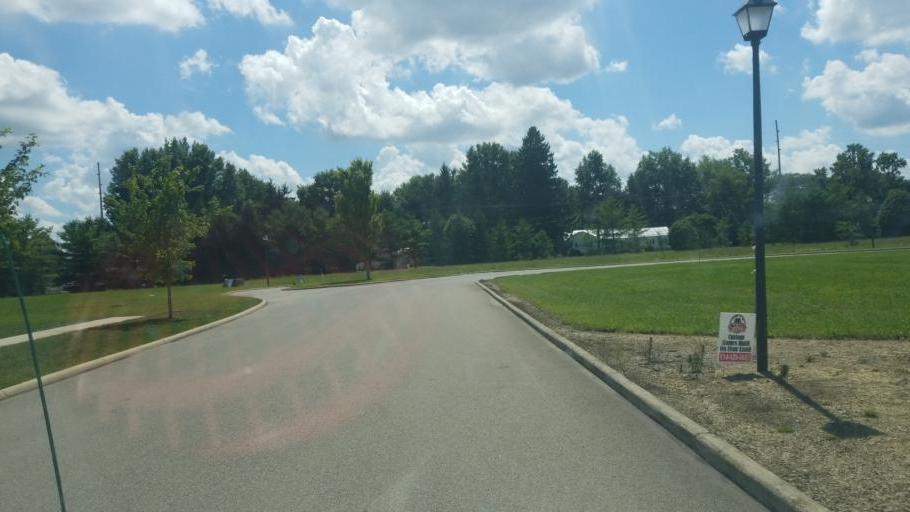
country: US
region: Ohio
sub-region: Marion County
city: Marion
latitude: 40.5651
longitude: -83.0940
